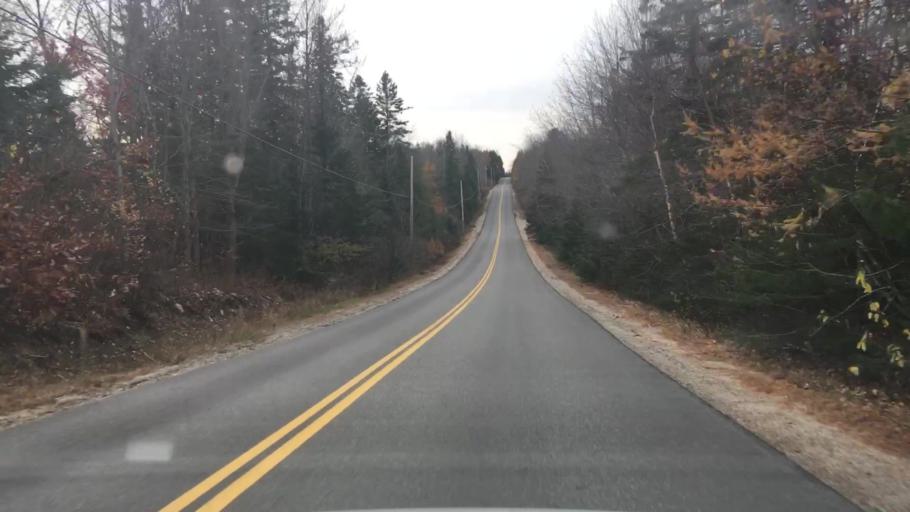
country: US
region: Maine
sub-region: Hancock County
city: Penobscot
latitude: 44.4518
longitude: -68.6372
